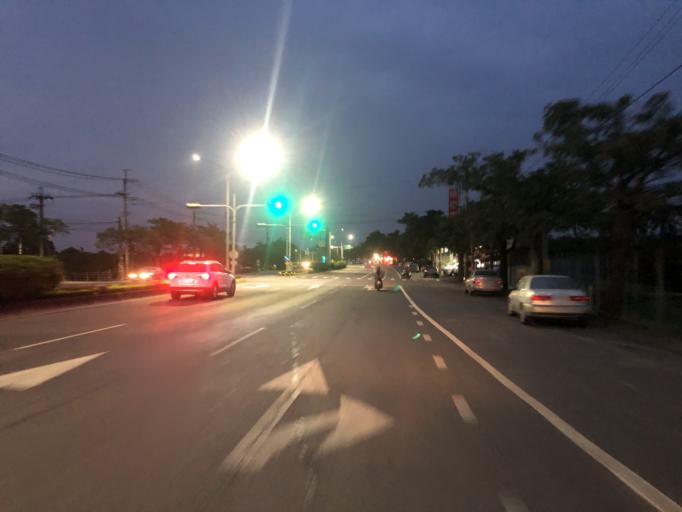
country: TW
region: Taiwan
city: Yujing
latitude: 23.1643
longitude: 120.3410
